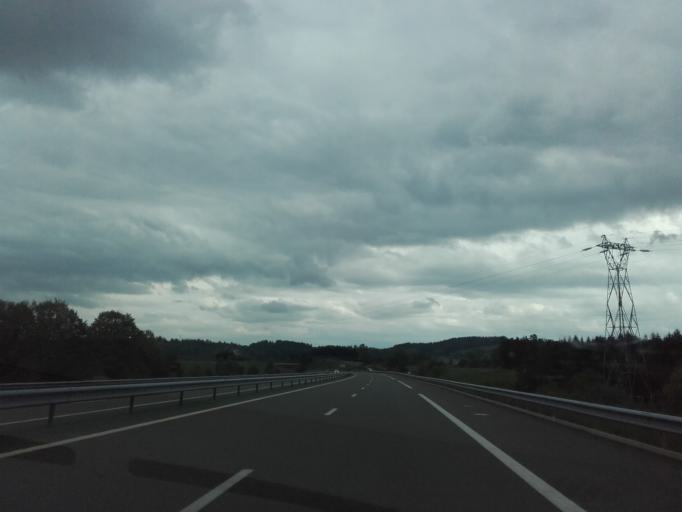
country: FR
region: Limousin
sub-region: Departement de la Correze
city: Meymac
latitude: 45.5111
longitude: 2.2185
